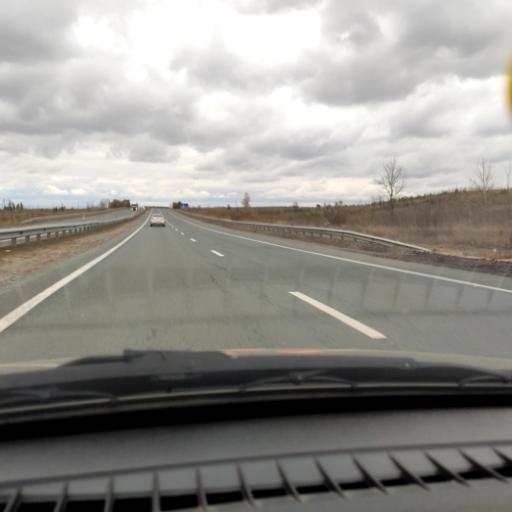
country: RU
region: Samara
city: Zhigulevsk
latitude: 53.5087
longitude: 49.5381
